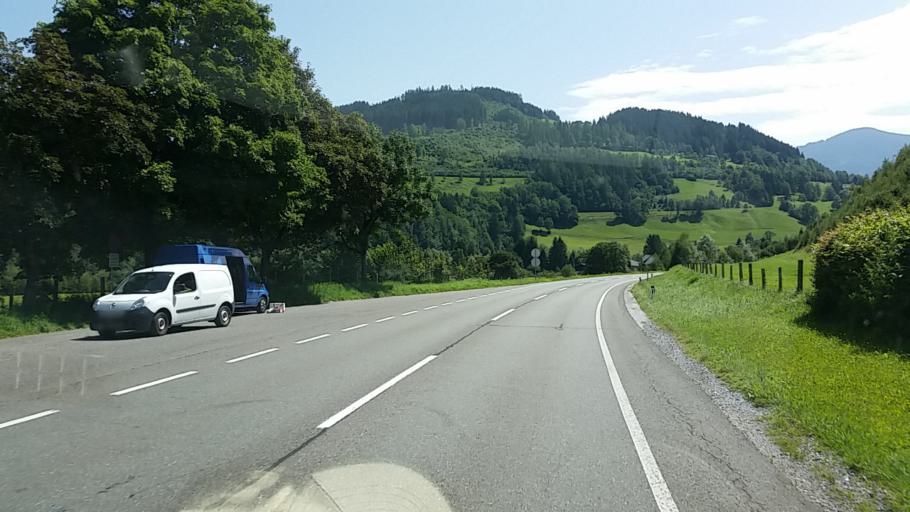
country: AT
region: Salzburg
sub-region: Politischer Bezirk Sankt Johann im Pongau
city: Pfarrwerfen
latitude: 47.4528
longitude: 13.2060
